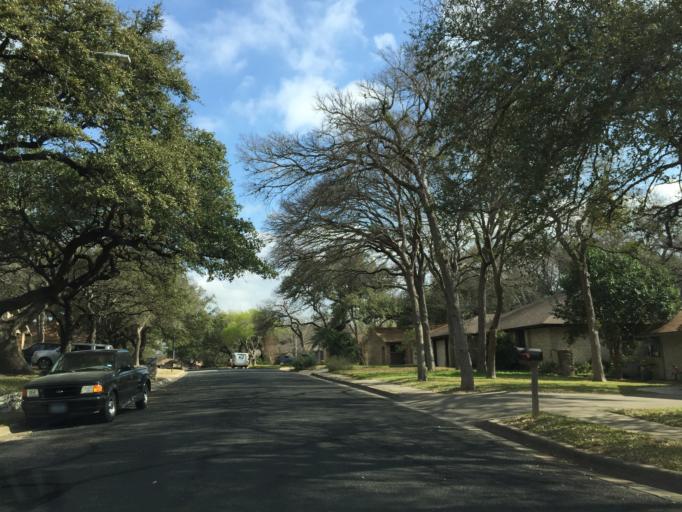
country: US
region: Texas
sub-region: Williamson County
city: Jollyville
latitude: 30.4123
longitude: -97.7347
